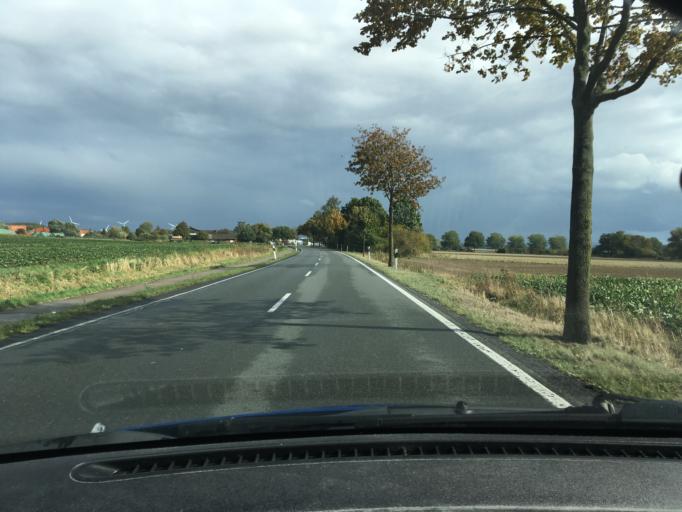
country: DE
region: Lower Saxony
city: Springe
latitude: 52.2107
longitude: 9.6084
